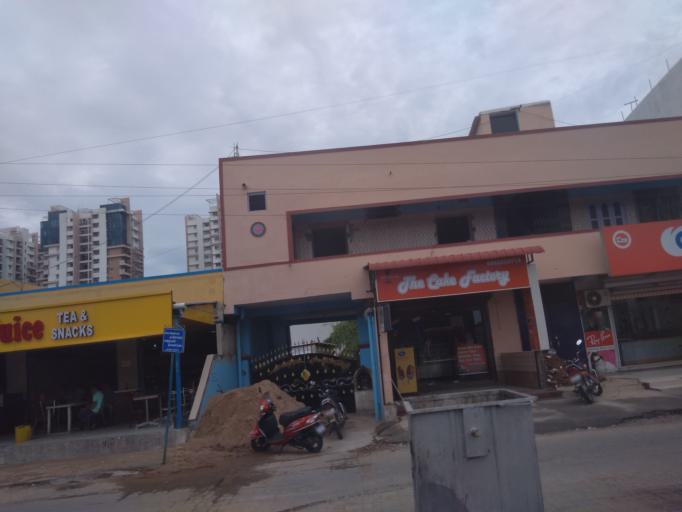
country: IN
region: Tamil Nadu
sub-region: Kancheepuram
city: Injambakkam
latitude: 12.8489
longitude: 80.2266
